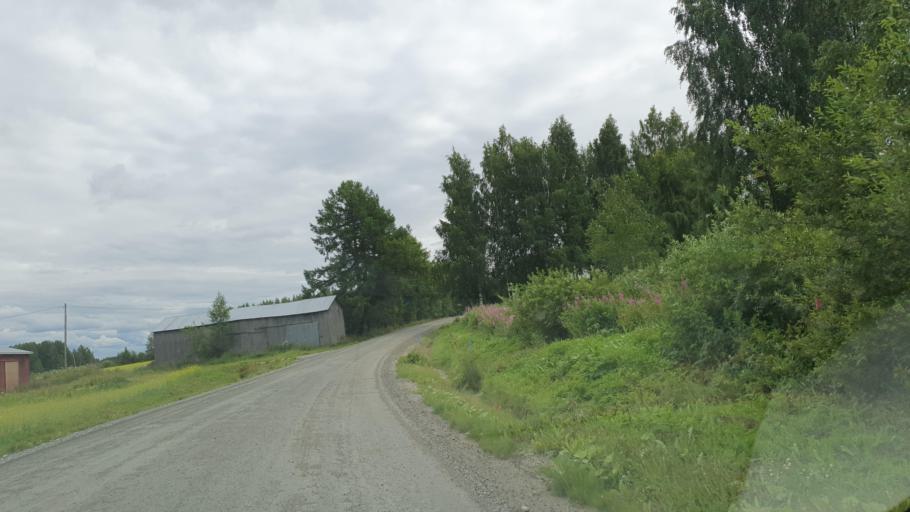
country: FI
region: Northern Savo
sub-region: Ylae-Savo
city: Iisalmi
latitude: 63.5359
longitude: 27.0849
